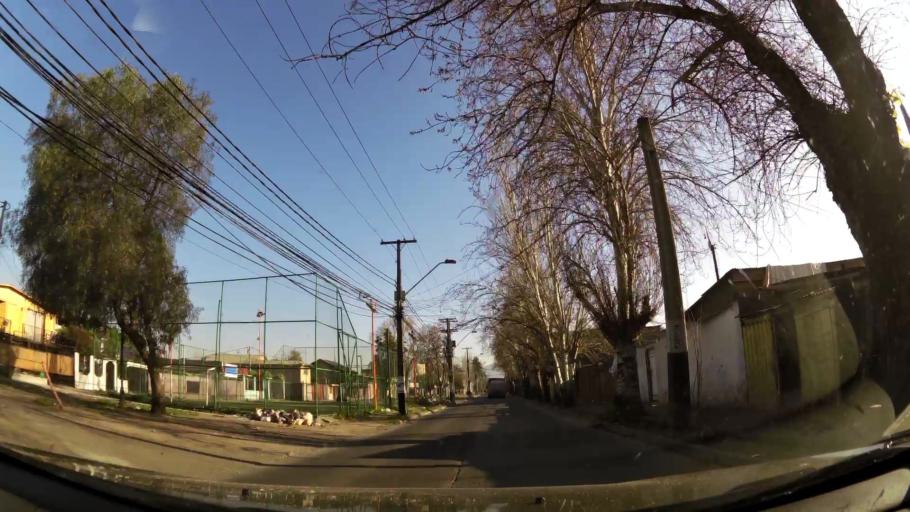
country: CL
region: Santiago Metropolitan
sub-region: Provincia de Santiago
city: Santiago
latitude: -33.3865
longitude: -70.6715
